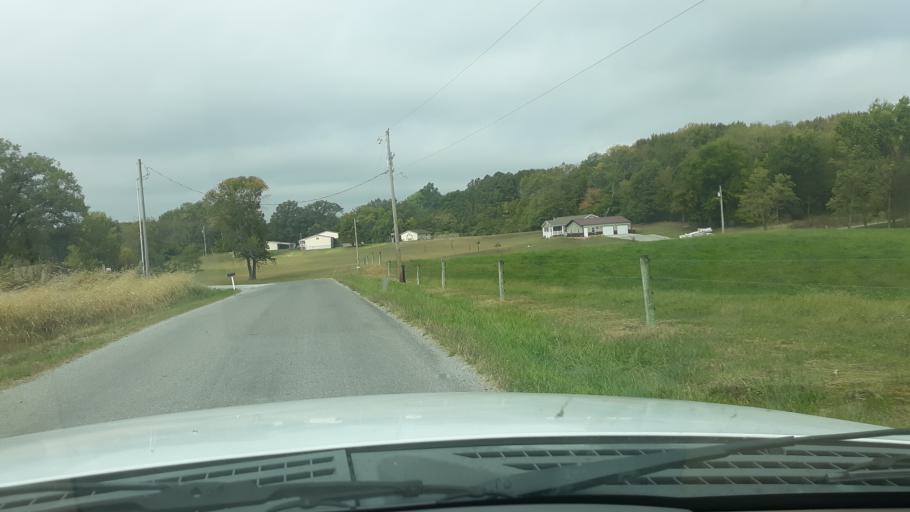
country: US
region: Illinois
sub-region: Saline County
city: Eldorado
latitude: 37.8369
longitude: -88.4877
